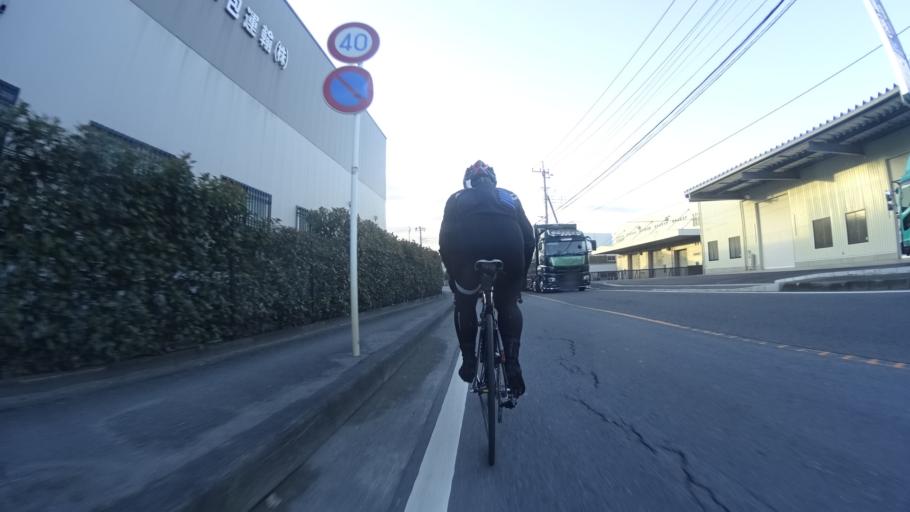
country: JP
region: Kanagawa
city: Atsugi
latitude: 35.4576
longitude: 139.3682
